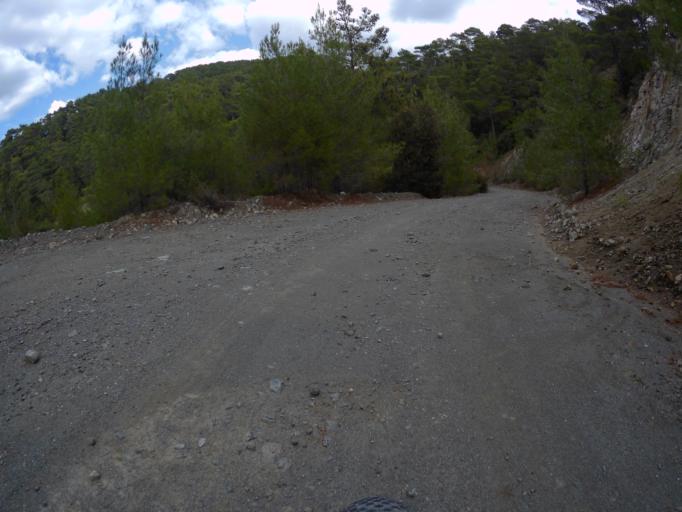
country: CY
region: Lefkosia
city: Kakopetria
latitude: 34.9008
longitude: 32.8444
